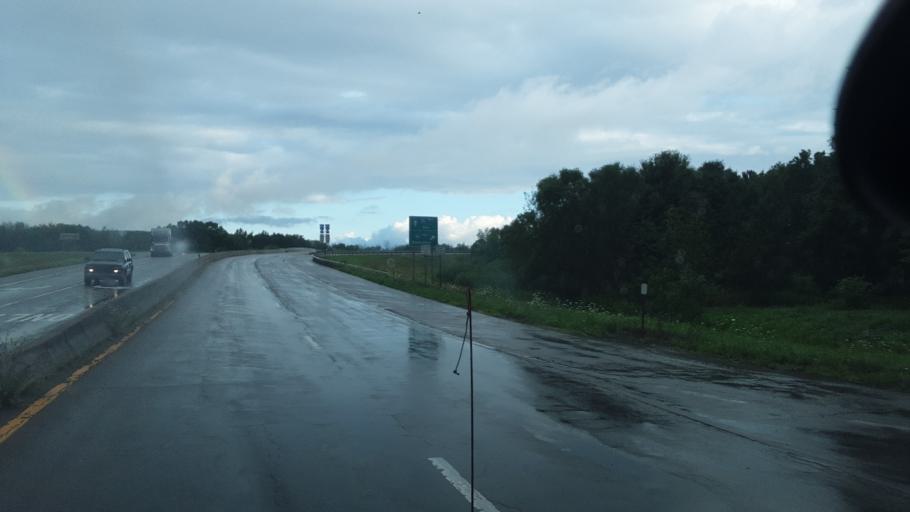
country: US
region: New York
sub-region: Chautauqua County
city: Falconer
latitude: 42.1276
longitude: -79.1886
